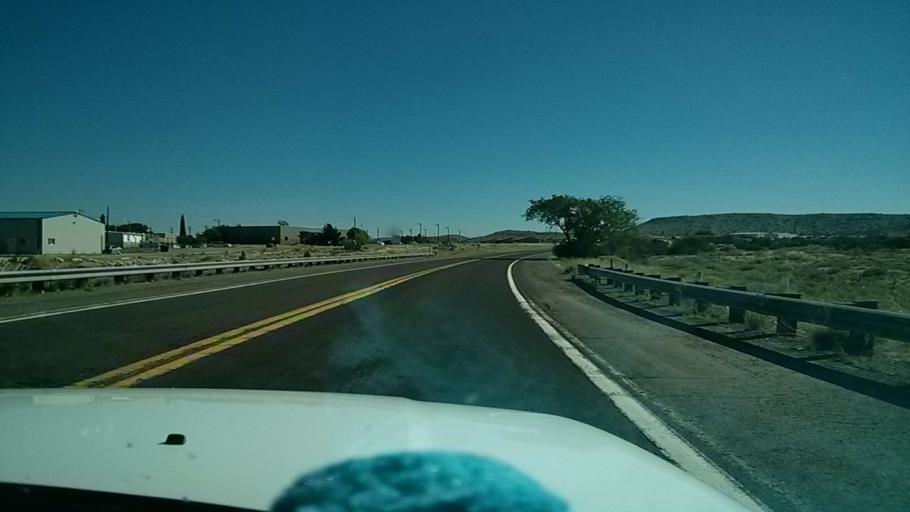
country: US
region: Arizona
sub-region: Mohave County
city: Peach Springs
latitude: 35.5363
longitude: -113.4197
